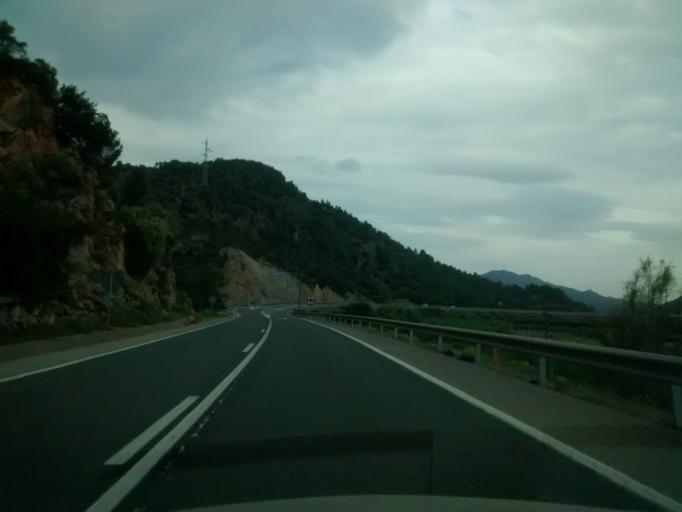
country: ES
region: Catalonia
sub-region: Provincia de Tarragona
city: Benifallet
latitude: 40.9789
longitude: 0.5160
